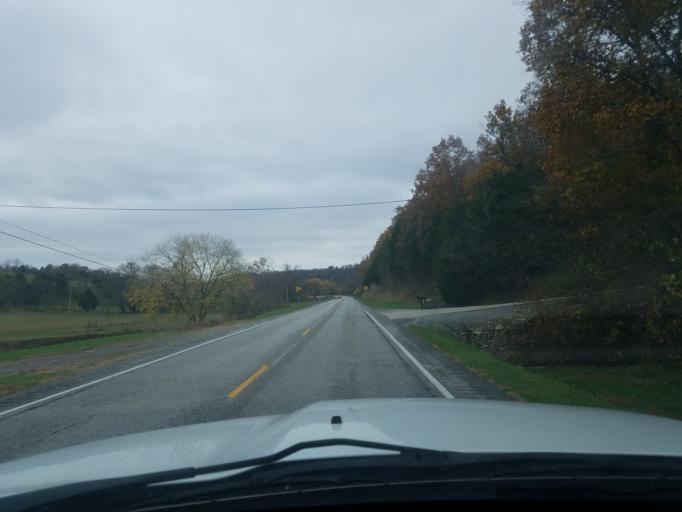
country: US
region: Kentucky
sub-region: Washington County
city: Springfield
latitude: 37.7562
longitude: -85.3098
